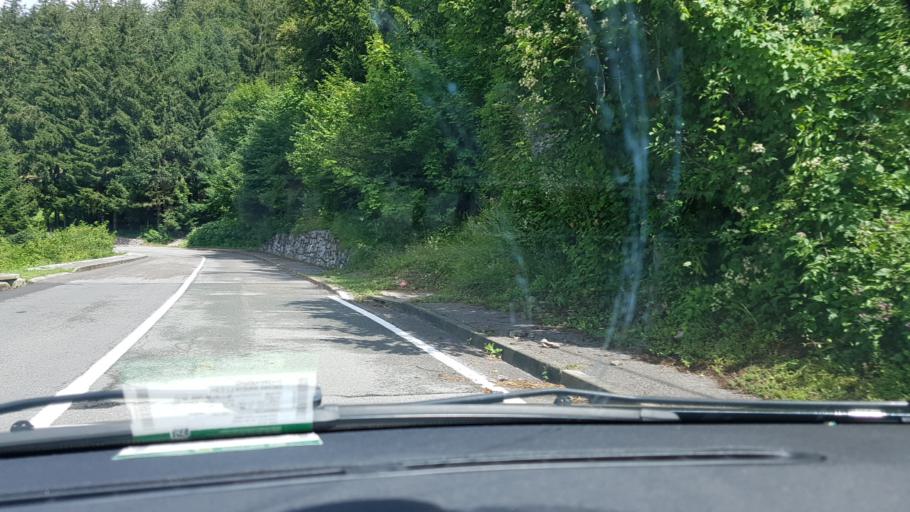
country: HR
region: Primorsko-Goranska
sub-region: Grad Delnice
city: Delnice
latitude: 45.3623
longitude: 14.7567
